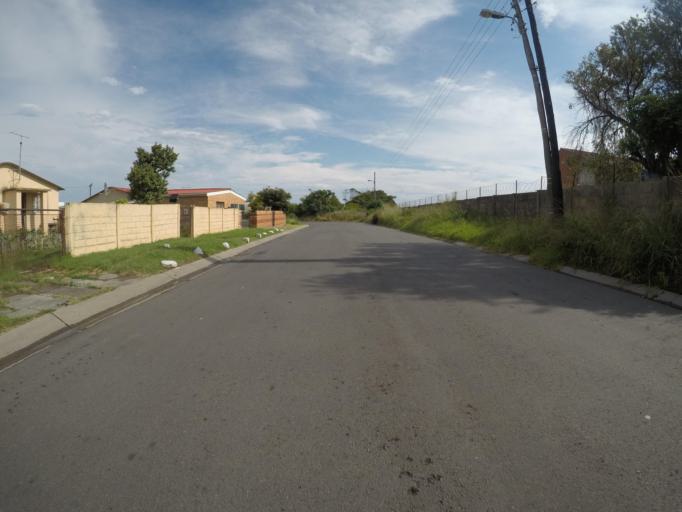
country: ZA
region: Eastern Cape
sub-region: Buffalo City Metropolitan Municipality
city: East London
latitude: -33.0231
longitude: 27.8724
